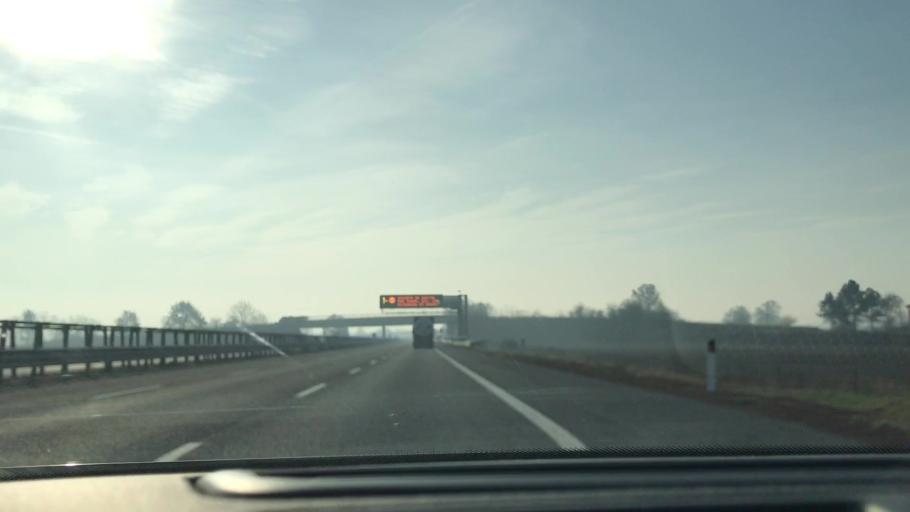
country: IT
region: Piedmont
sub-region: Provincia di Alessandria
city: Alessandria
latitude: 44.8902
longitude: 8.5688
